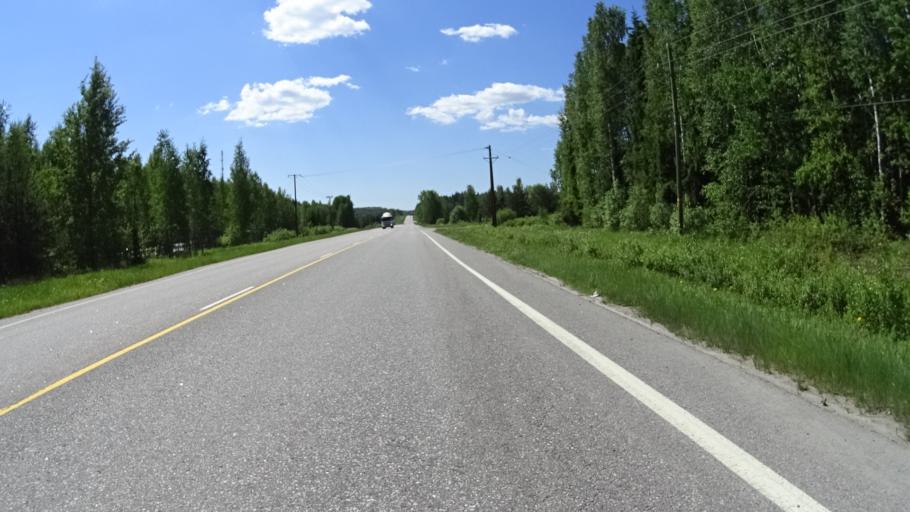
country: FI
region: Uusimaa
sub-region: Helsinki
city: Nurmijaervi
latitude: 60.4078
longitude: 24.8211
